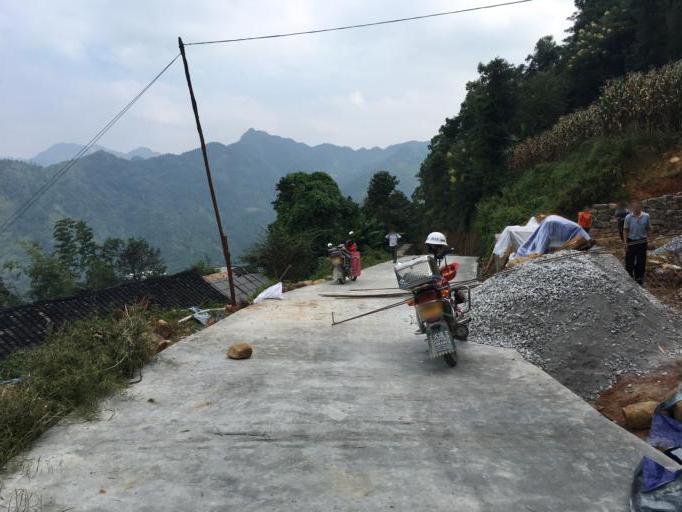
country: CN
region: Guangxi Zhuangzu Zizhiqu
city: Tongle
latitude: 25.2975
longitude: 106.1635
